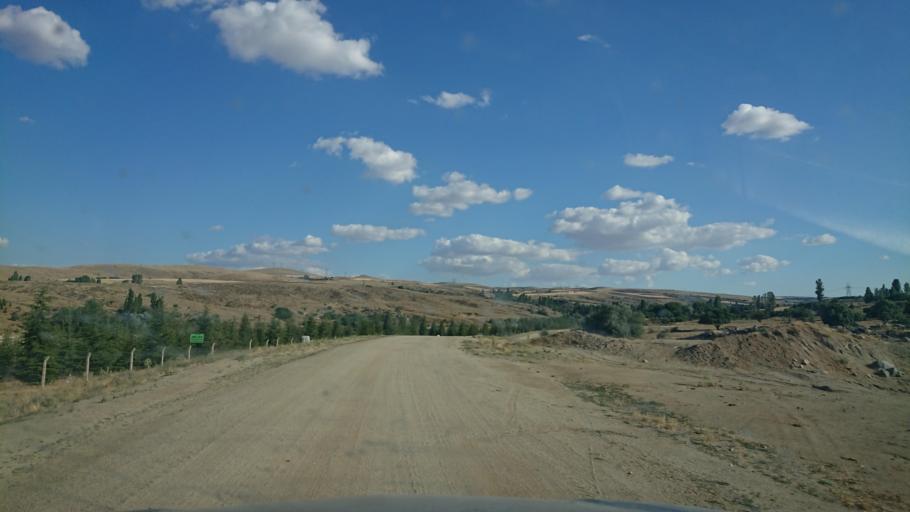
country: TR
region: Aksaray
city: Sariyahsi
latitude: 38.9489
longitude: 33.8810
